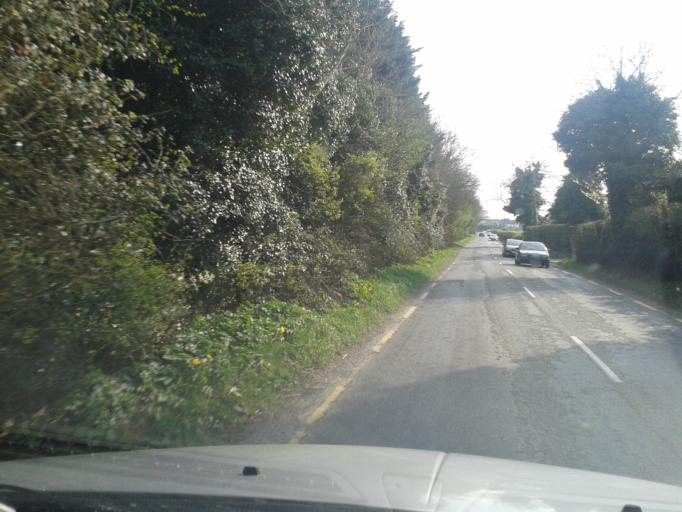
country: IE
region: Leinster
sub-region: Fingal County
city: Swords
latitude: 53.4428
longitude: -6.2458
